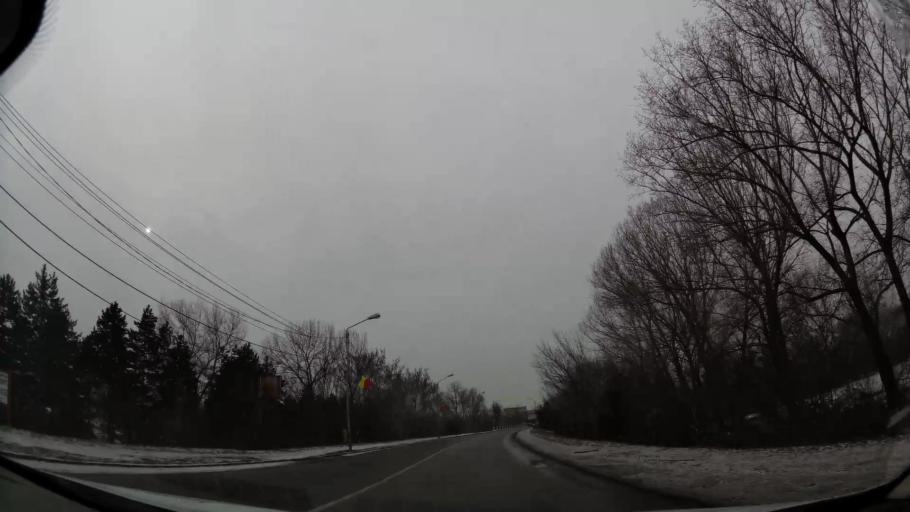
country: RO
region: Dambovita
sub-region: Municipiul Targoviste
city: Targoviste
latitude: 44.9395
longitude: 25.4574
